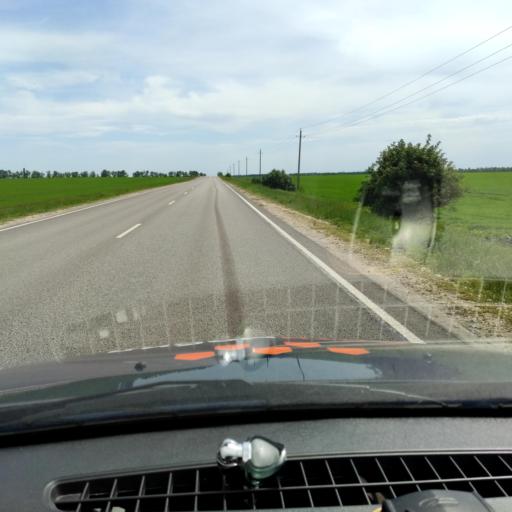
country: RU
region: Voronezj
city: Novaya Usman'
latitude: 51.5628
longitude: 39.3758
